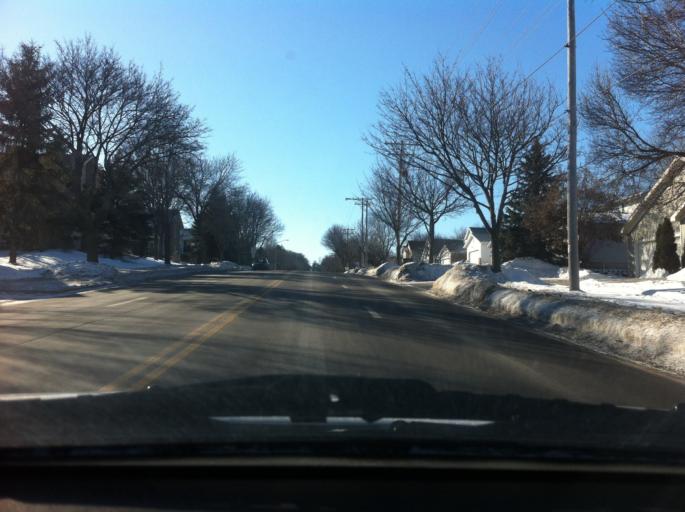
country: US
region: Wisconsin
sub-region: Dane County
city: Middleton
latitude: 43.0802
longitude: -89.5023
